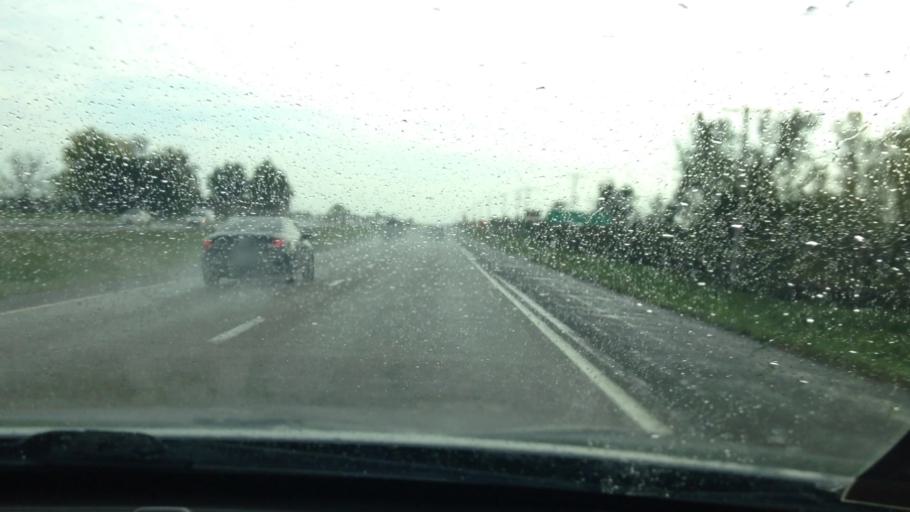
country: US
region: Kansas
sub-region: Leavenworth County
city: Basehor
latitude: 39.1744
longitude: -94.9007
